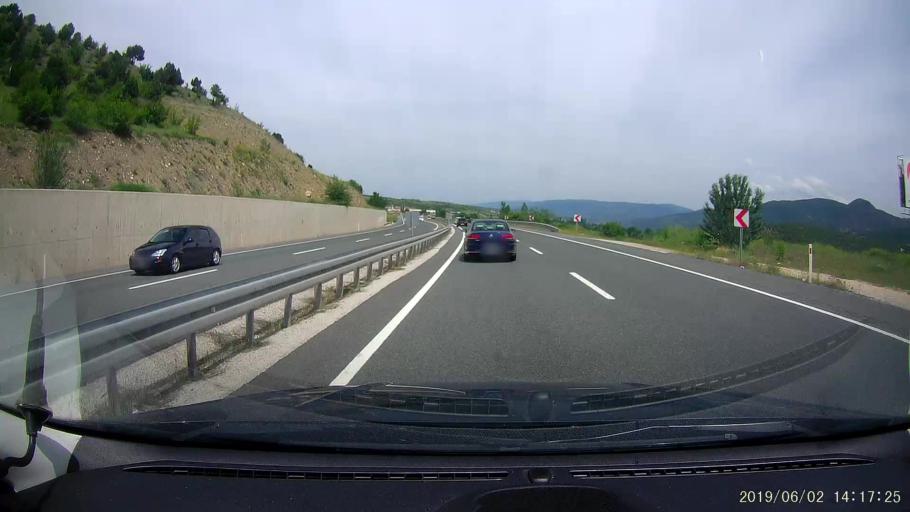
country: TR
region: Kastamonu
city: Tosya
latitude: 40.9539
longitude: 33.9314
